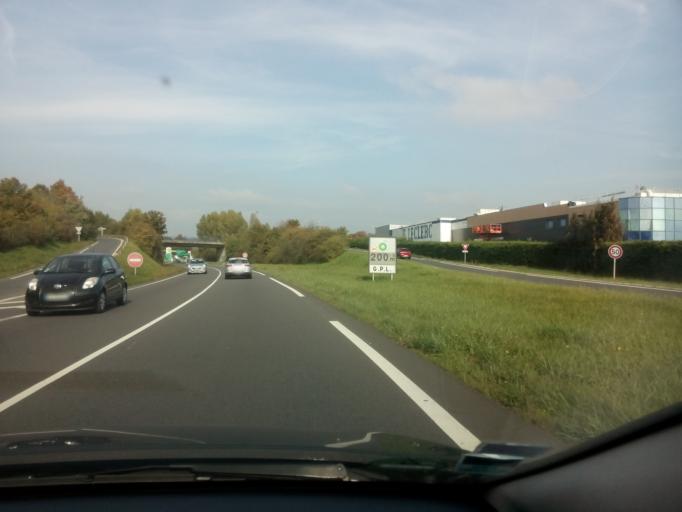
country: FR
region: Ile-de-France
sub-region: Departement de l'Essonne
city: Palaiseau
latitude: 48.7282
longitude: 2.2437
